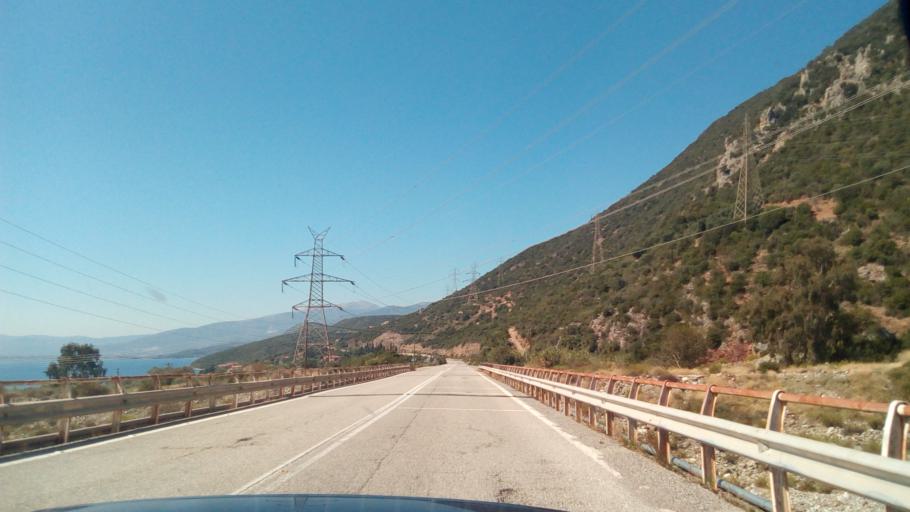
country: GR
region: West Greece
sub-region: Nomos Achaias
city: Kamarai
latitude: 38.3977
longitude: 22.0056
